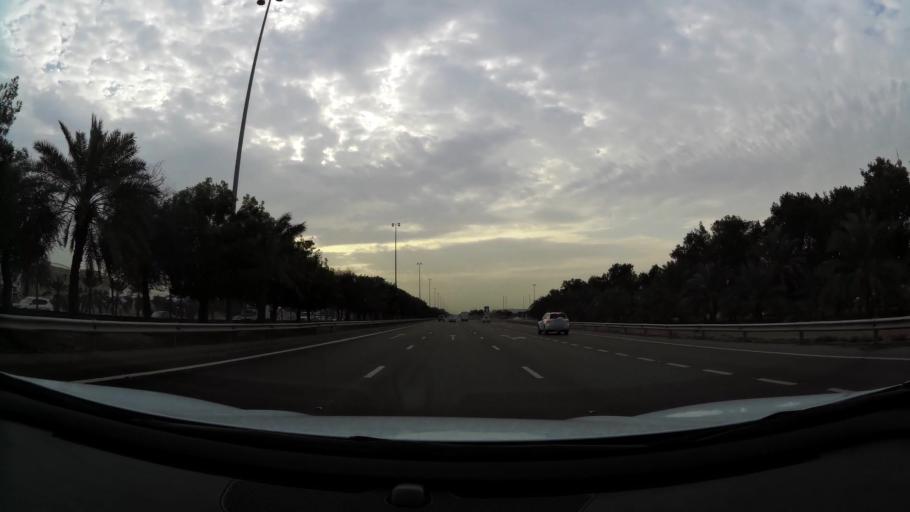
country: AE
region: Abu Dhabi
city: Abu Dhabi
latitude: 24.2961
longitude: 54.6276
